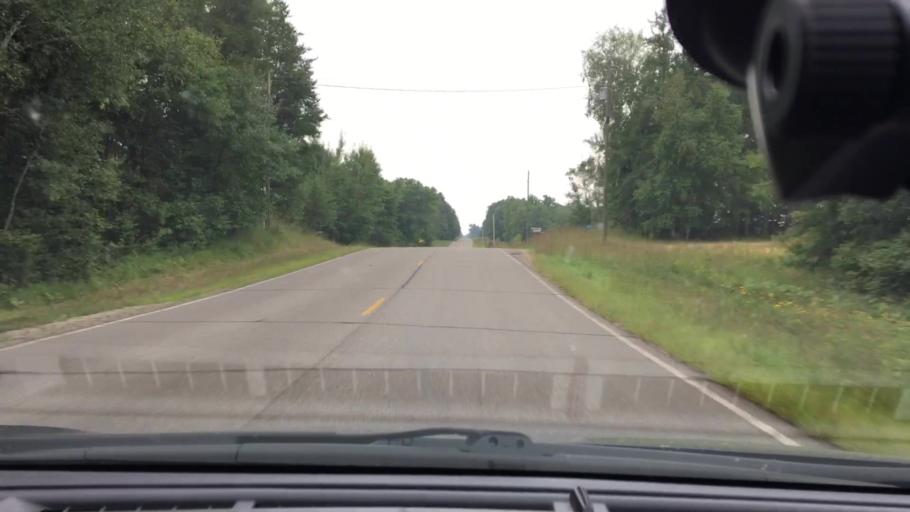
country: US
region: Minnesota
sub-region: Crow Wing County
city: Cross Lake
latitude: 46.6544
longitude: -94.0094
